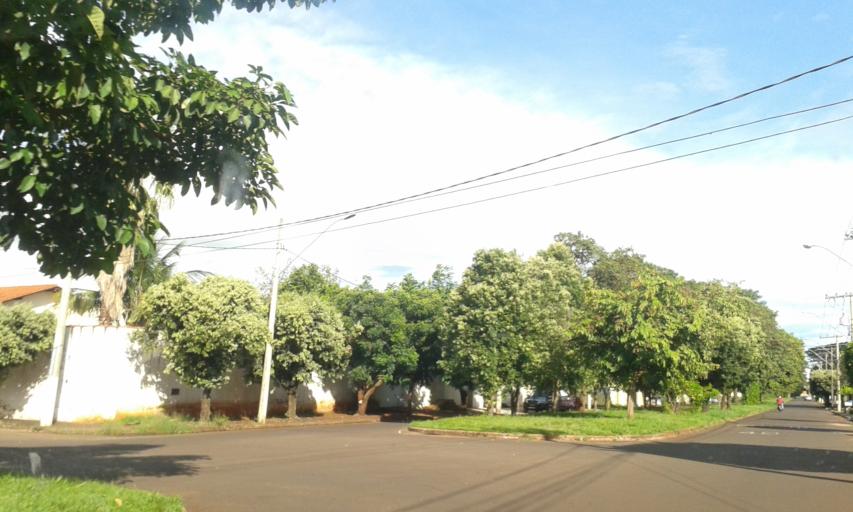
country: BR
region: Minas Gerais
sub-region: Ituiutaba
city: Ituiutaba
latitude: -18.9683
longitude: -49.4505
